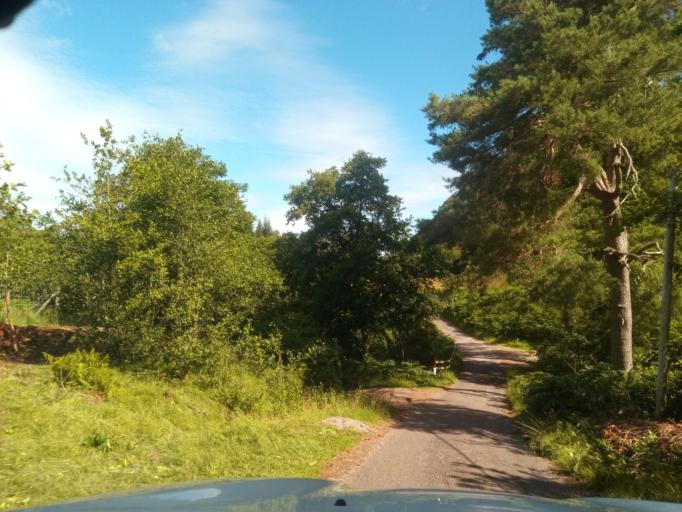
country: GB
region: Scotland
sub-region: Argyll and Bute
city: Isle Of Mull
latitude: 56.7745
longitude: -5.8245
